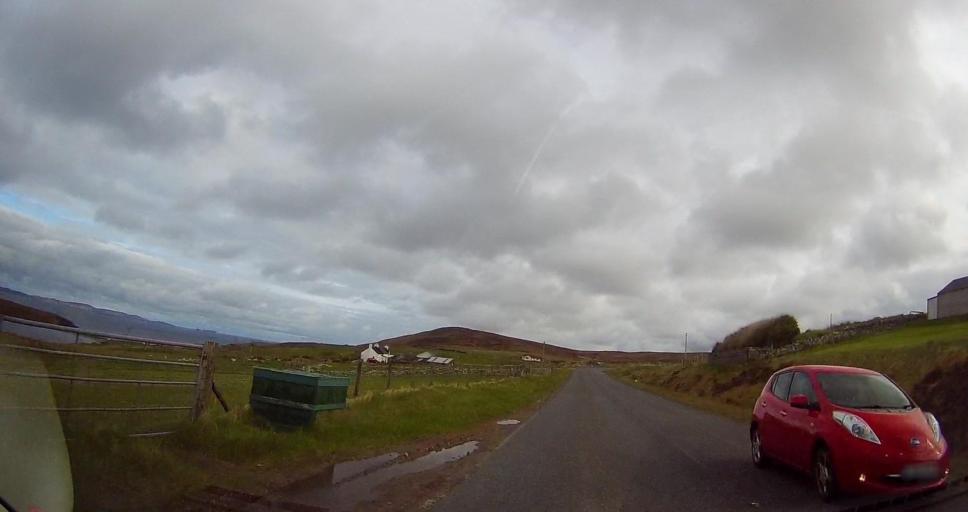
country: GB
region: Scotland
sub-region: Shetland Islands
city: Shetland
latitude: 60.5158
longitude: -1.1655
